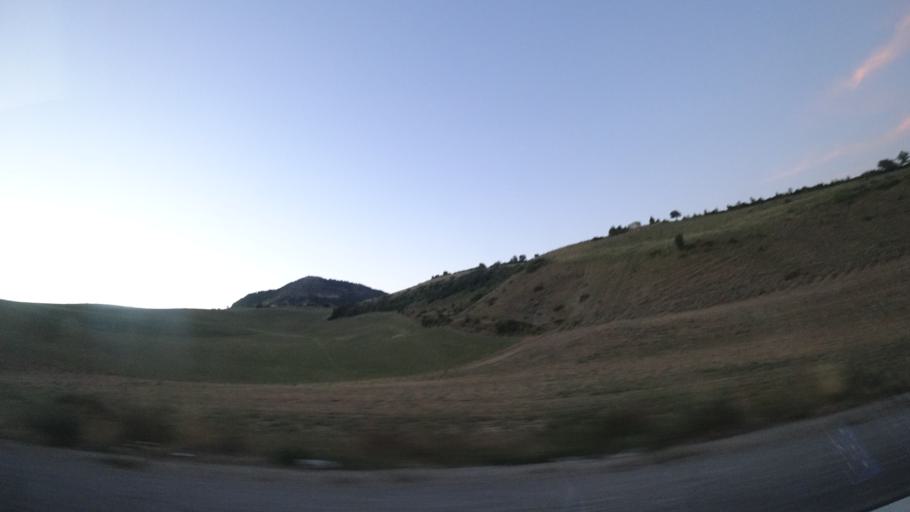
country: FR
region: Midi-Pyrenees
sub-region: Departement de l'Aveyron
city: Millau
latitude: 44.1215
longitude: 3.0620
